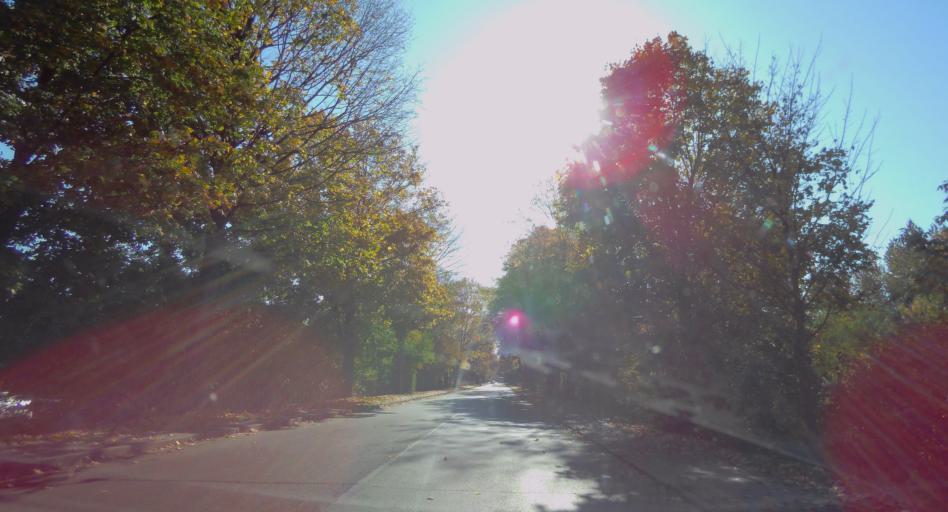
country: PL
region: Subcarpathian Voivodeship
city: Nowa Sarzyna
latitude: 50.3243
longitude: 22.3396
